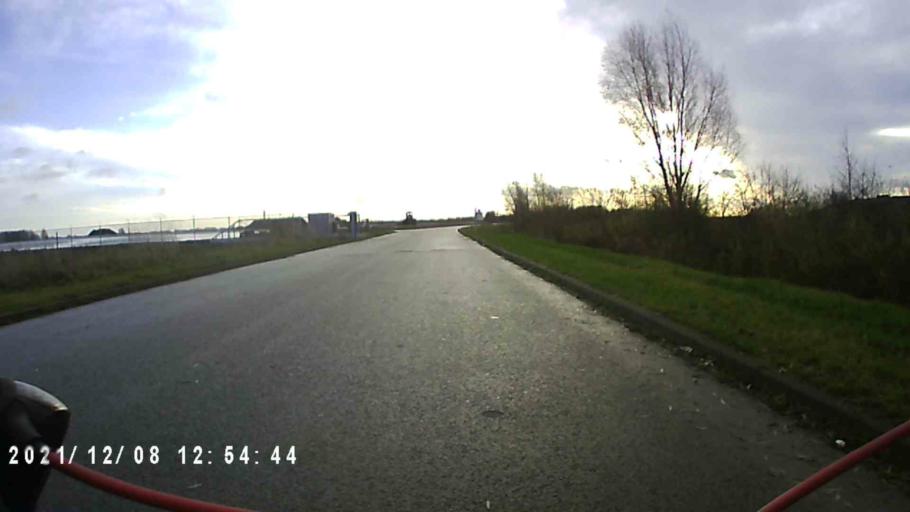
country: NL
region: Groningen
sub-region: Gemeente Haren
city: Haren
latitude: 53.1993
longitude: 6.6295
